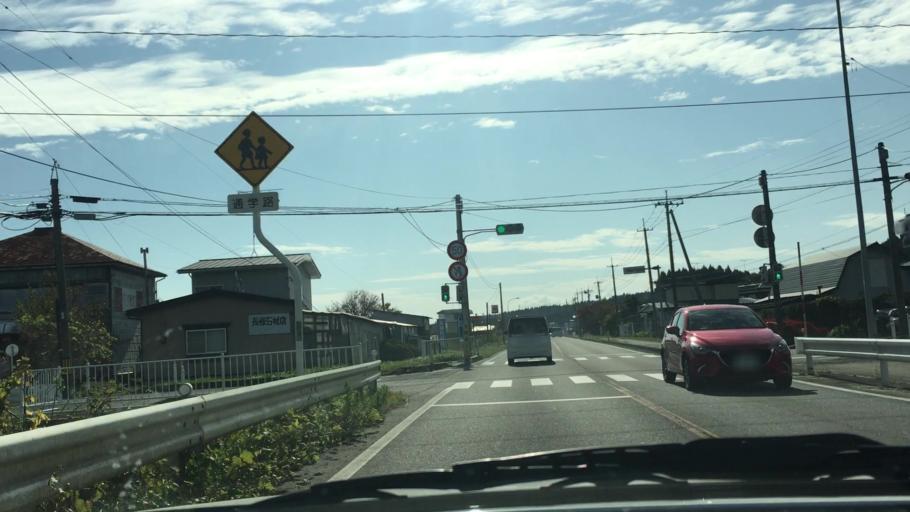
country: JP
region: Aomori
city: Hachinohe
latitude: 40.4233
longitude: 141.6984
